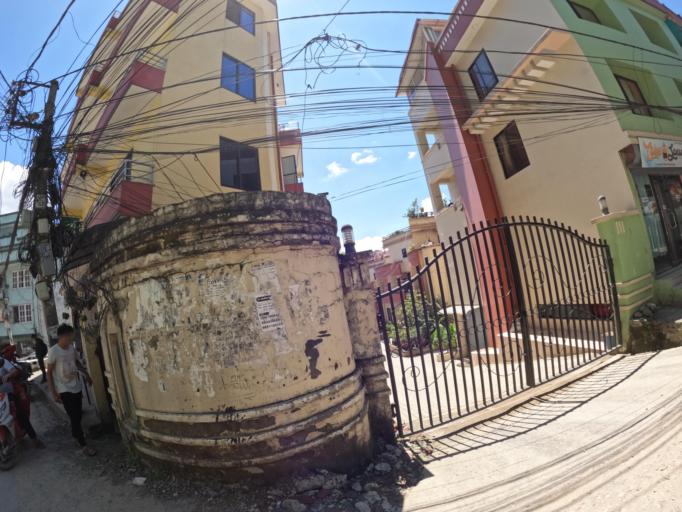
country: NP
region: Central Region
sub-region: Bagmati Zone
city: Kathmandu
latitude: 27.7396
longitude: 85.3237
